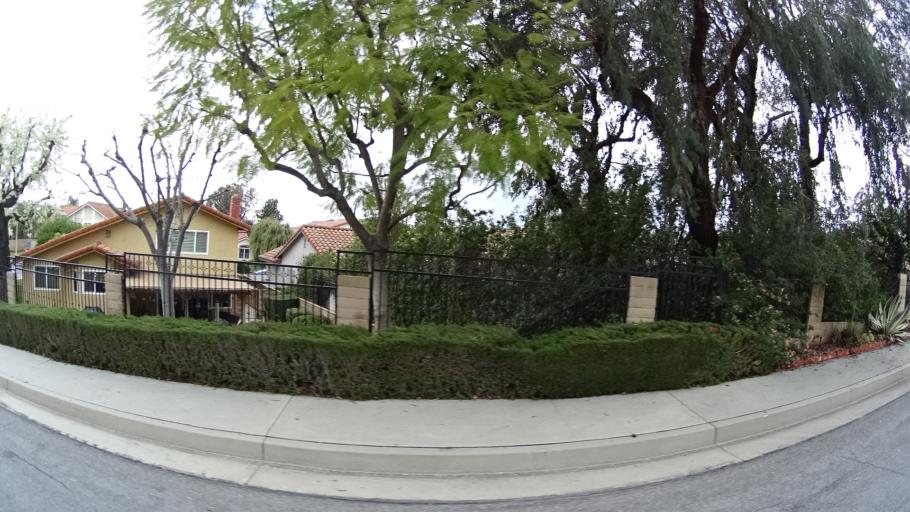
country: US
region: California
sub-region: Orange County
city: Villa Park
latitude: 33.8358
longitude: -117.7522
